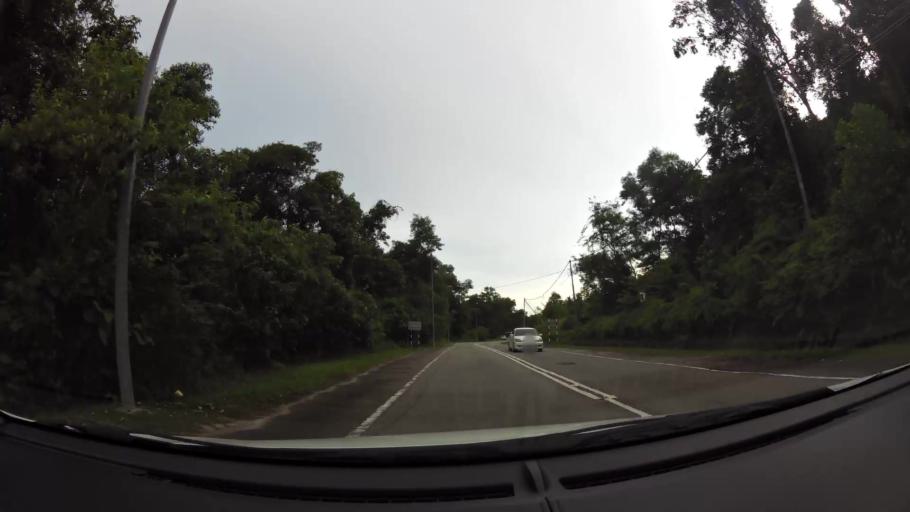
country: BN
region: Brunei and Muara
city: Bandar Seri Begawan
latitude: 4.9192
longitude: 115.0078
